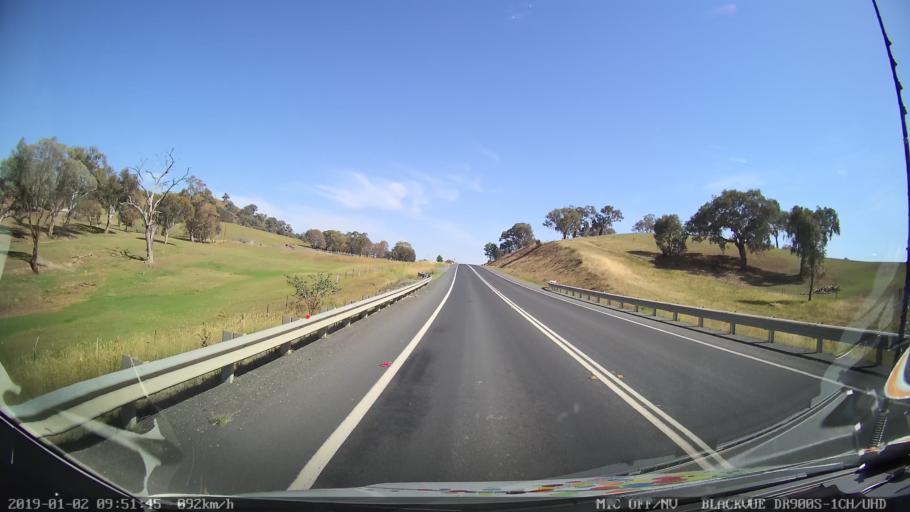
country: AU
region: New South Wales
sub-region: Tumut Shire
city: Tumut
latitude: -35.2696
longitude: 148.2116
